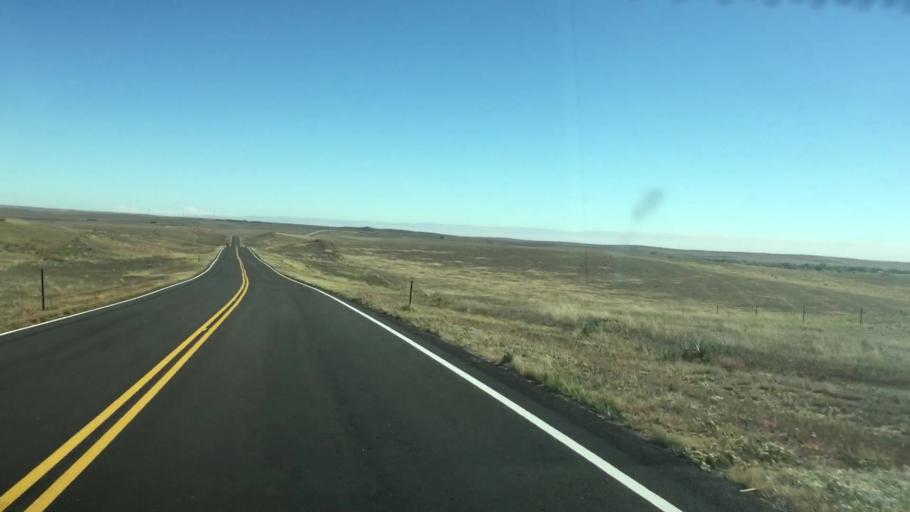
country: US
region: Colorado
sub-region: Lincoln County
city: Limon
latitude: 39.2974
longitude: -103.8540
